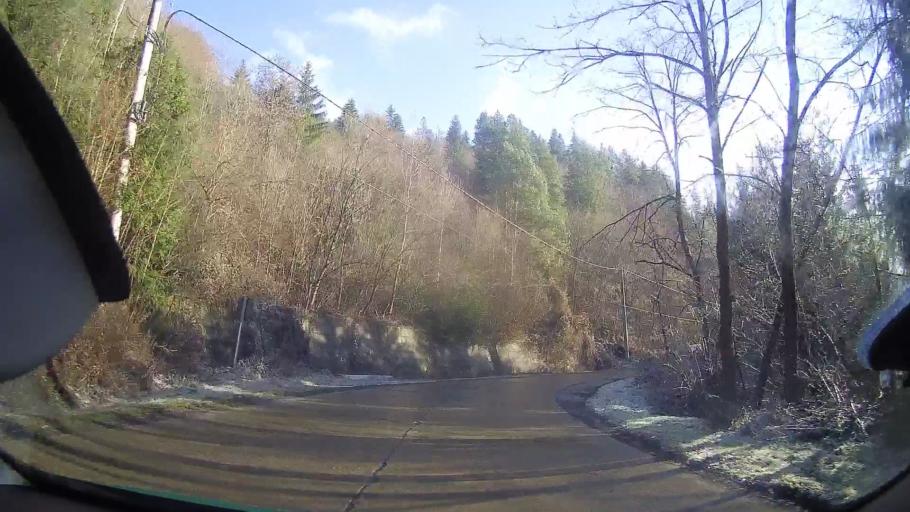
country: RO
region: Alba
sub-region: Comuna Vadu Motilor
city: Vadu Motilor
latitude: 46.3931
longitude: 22.9934
